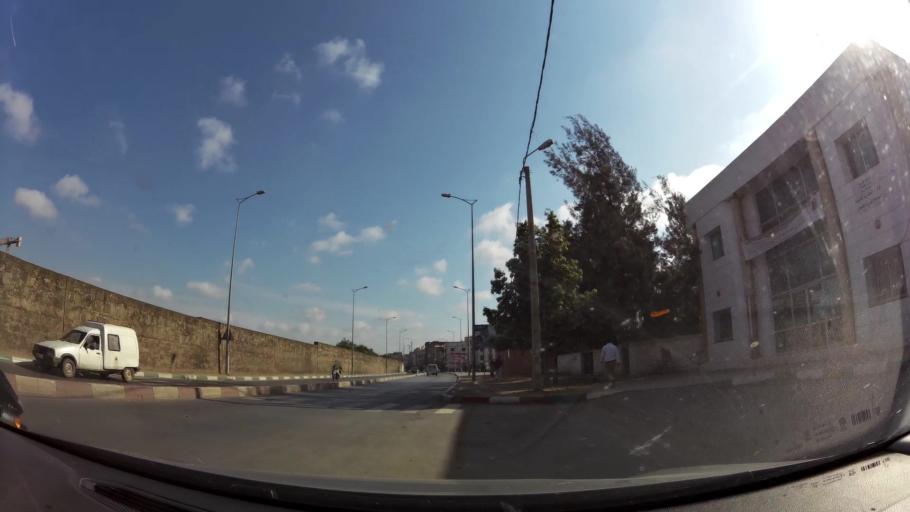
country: MA
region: Rabat-Sale-Zemmour-Zaer
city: Sale
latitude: 34.0555
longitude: -6.7722
